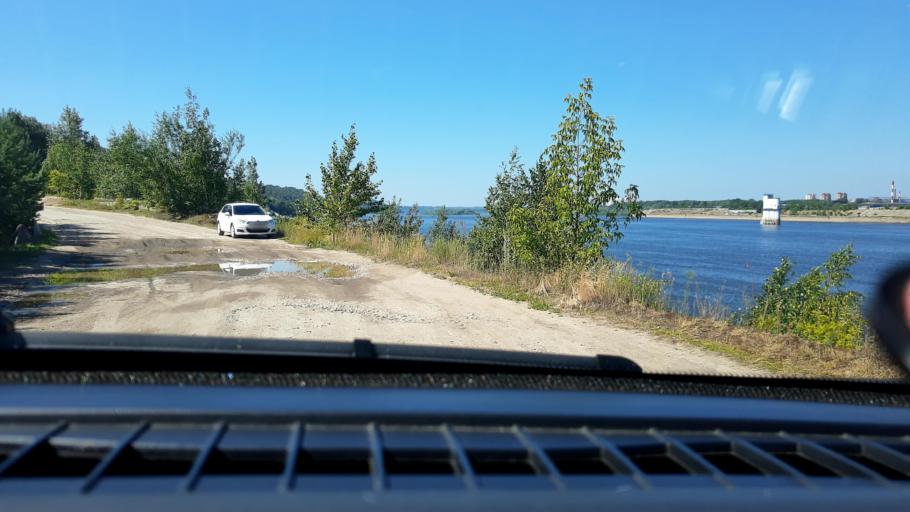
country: RU
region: Nizjnij Novgorod
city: Nizhniy Novgorod
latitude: 56.2292
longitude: 43.9197
